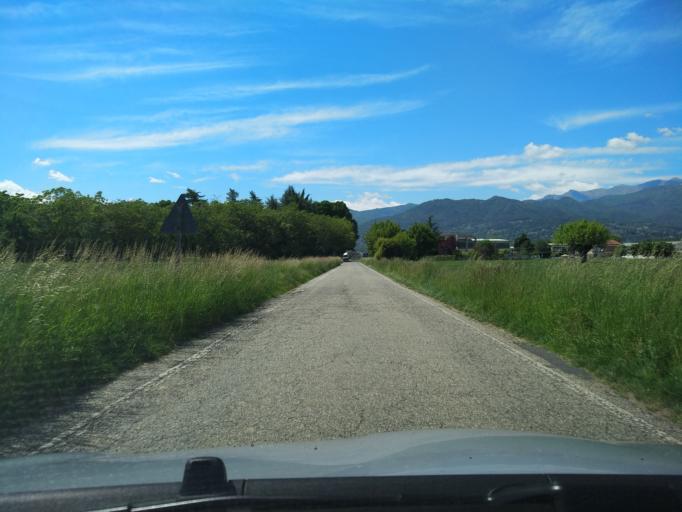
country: IT
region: Piedmont
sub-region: Provincia di Torino
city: Frossasco
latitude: 44.9105
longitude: 7.3675
